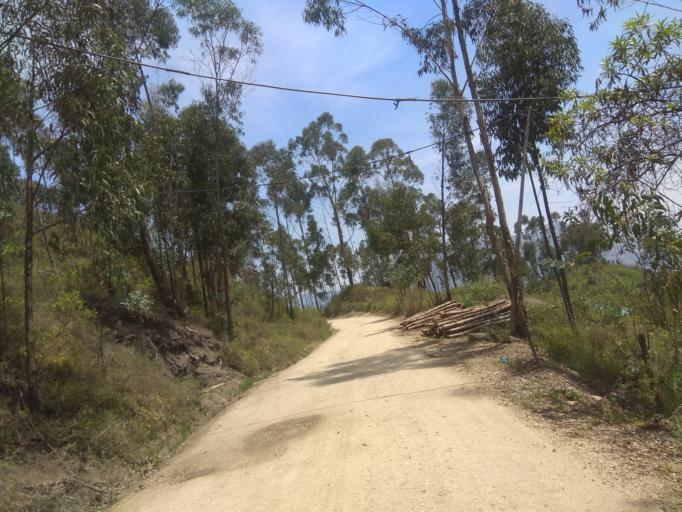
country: CO
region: Boyaca
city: Socha Viejo
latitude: 5.9809
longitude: -72.7319
